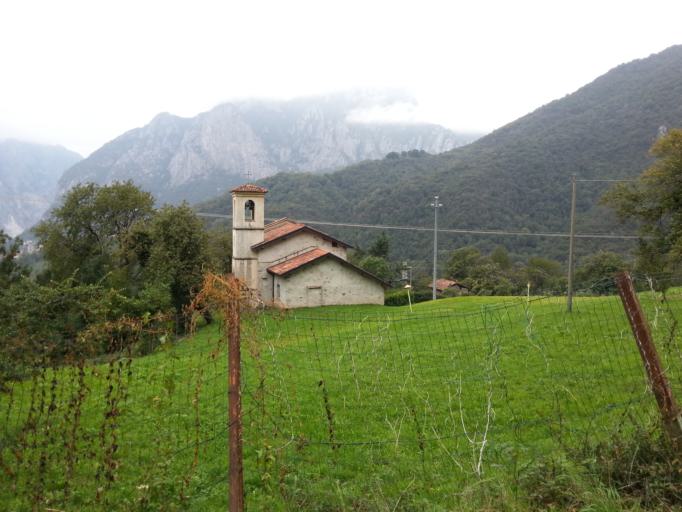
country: IT
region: Lombardy
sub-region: Provincia di Lecco
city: Ballabio
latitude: 45.8690
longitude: 9.4300
